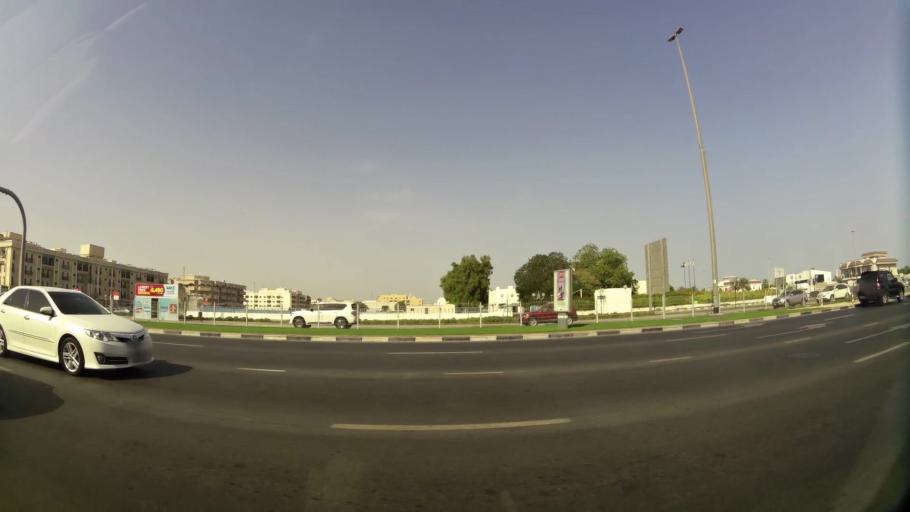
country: AE
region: Ash Shariqah
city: Sharjah
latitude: 25.2854
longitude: 55.3514
